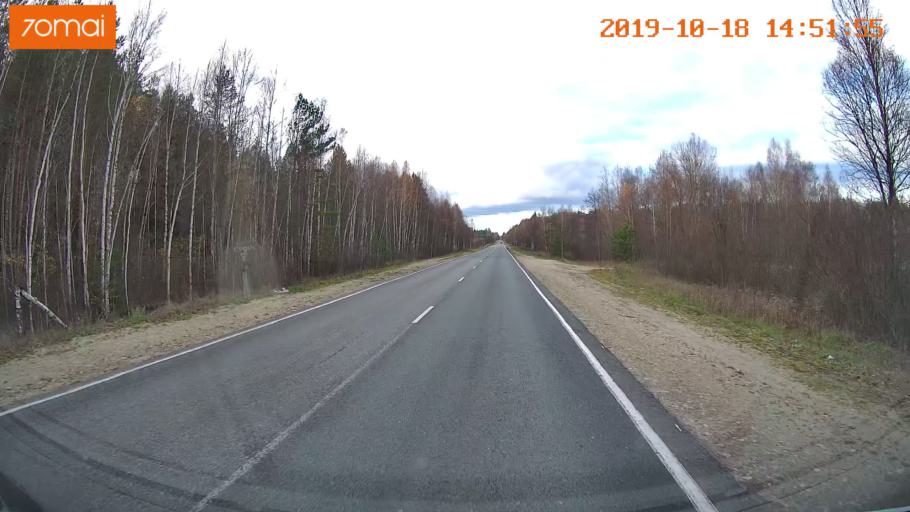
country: RU
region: Vladimir
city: Kurlovo
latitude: 55.4267
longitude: 40.6408
